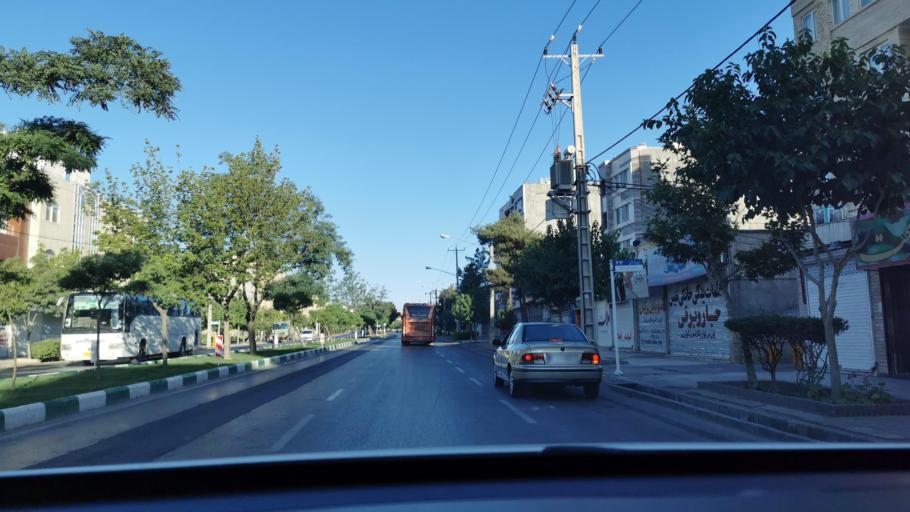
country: IR
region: Razavi Khorasan
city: Mashhad
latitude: 36.3523
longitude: 59.4958
